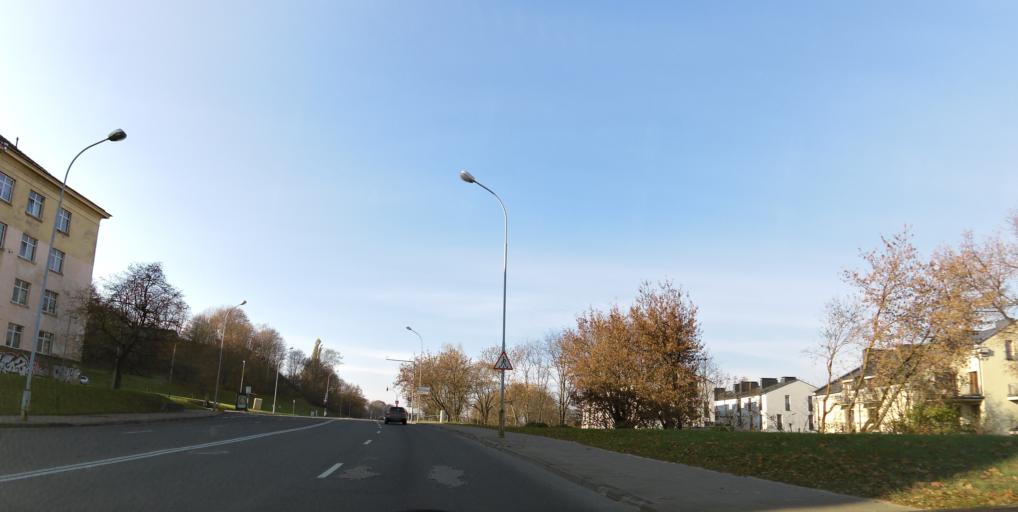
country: LT
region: Vilnius County
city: Rasos
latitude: 54.6771
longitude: 25.3047
